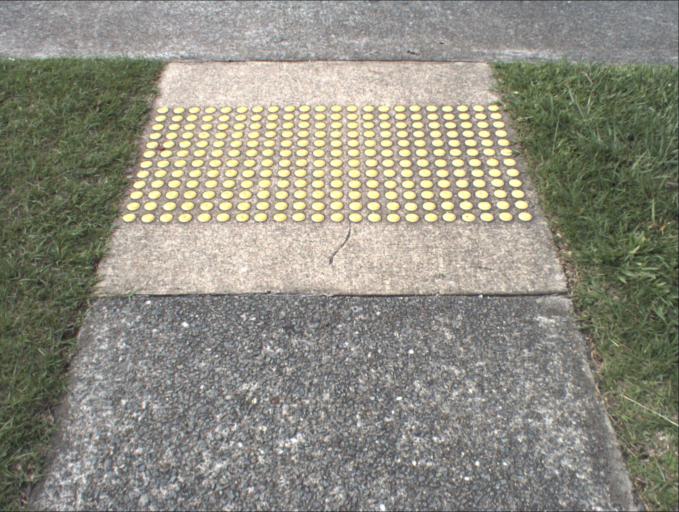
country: AU
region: Queensland
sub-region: Brisbane
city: Sunnybank Hills
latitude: -27.6658
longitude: 153.0336
